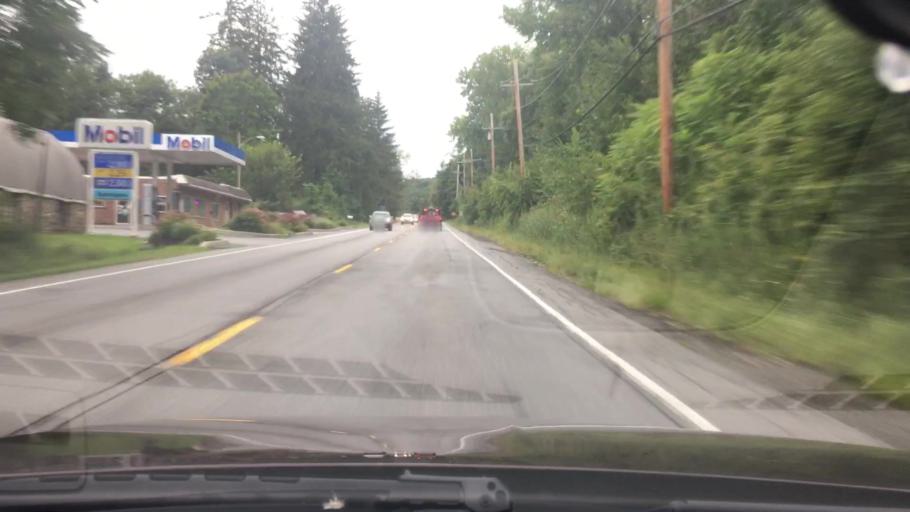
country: US
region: New York
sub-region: Dutchess County
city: Millbrook
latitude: 41.7818
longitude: -73.7592
